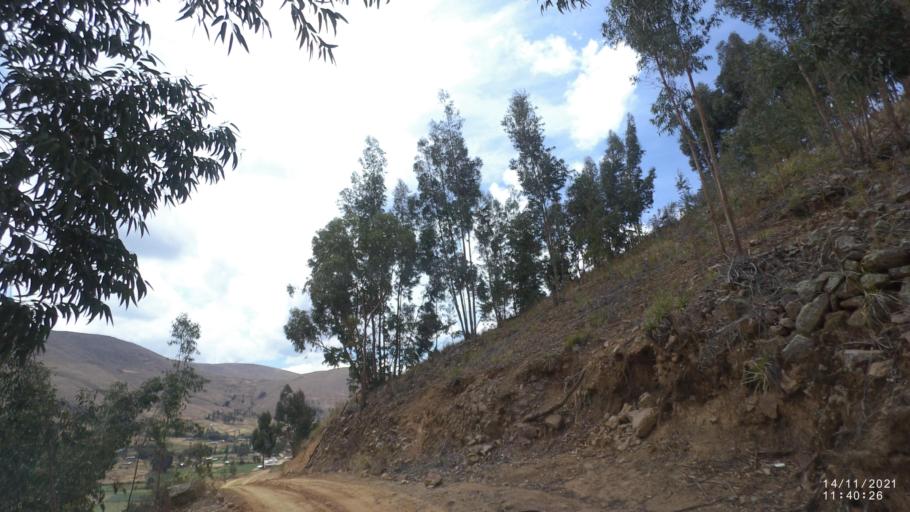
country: BO
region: Cochabamba
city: Colomi
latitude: -17.3515
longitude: -65.9963
